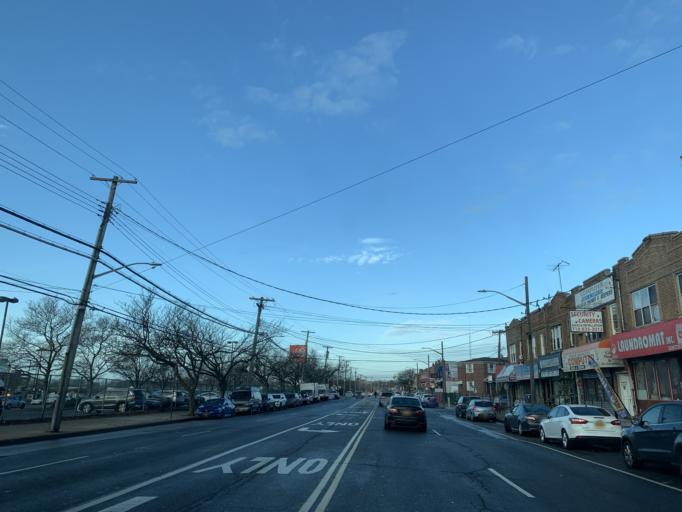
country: US
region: New York
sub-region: Queens County
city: Borough of Queens
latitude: 40.6773
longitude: -73.8258
